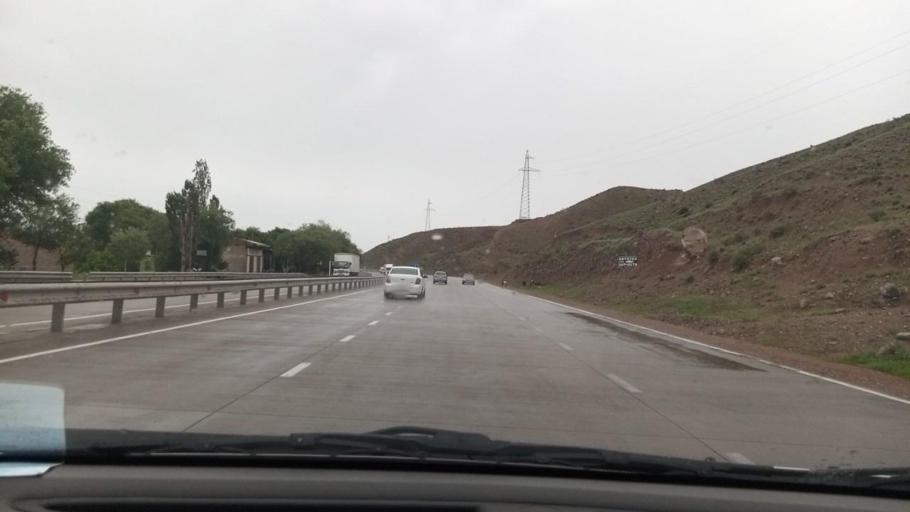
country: UZ
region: Namangan
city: Pop Shahri
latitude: 40.9479
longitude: 70.6813
